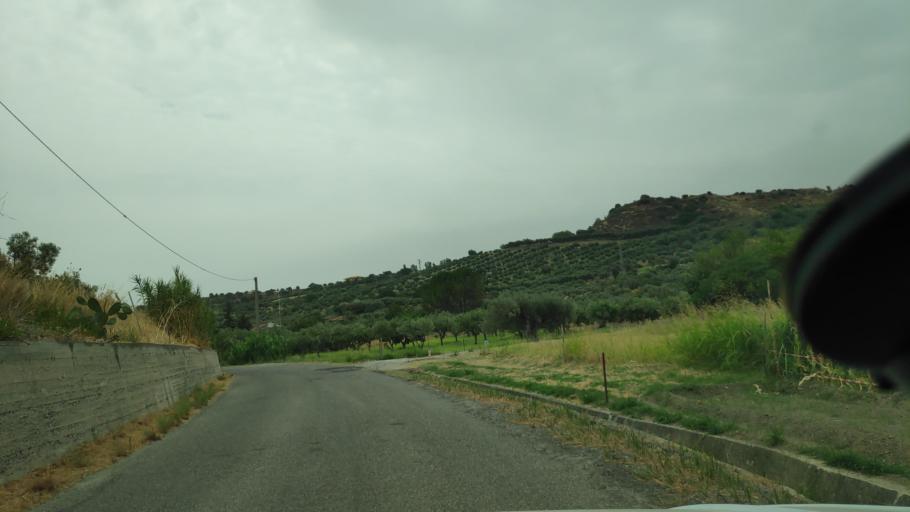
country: IT
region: Calabria
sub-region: Provincia di Catanzaro
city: Martelli-Laganosa
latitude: 38.6645
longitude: 16.5304
